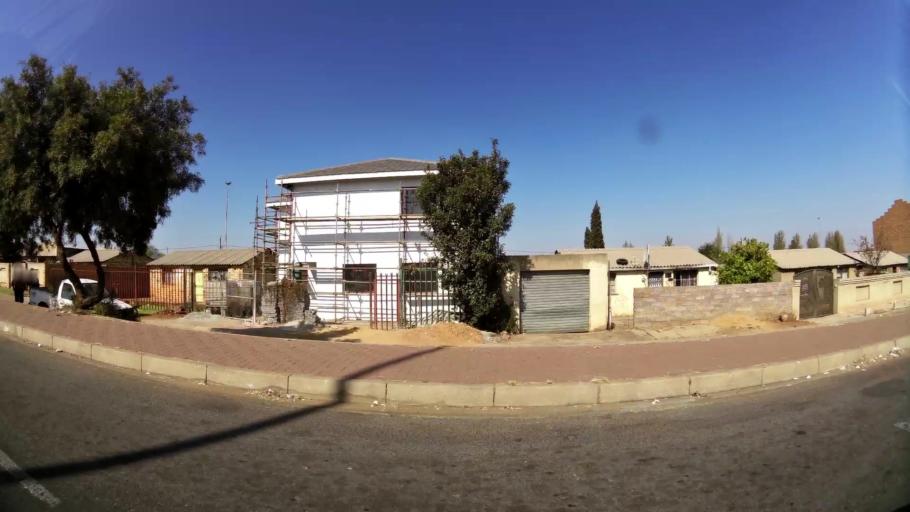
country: ZA
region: Gauteng
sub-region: City of Johannesburg Metropolitan Municipality
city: Soweto
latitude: -26.2838
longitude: 27.8555
